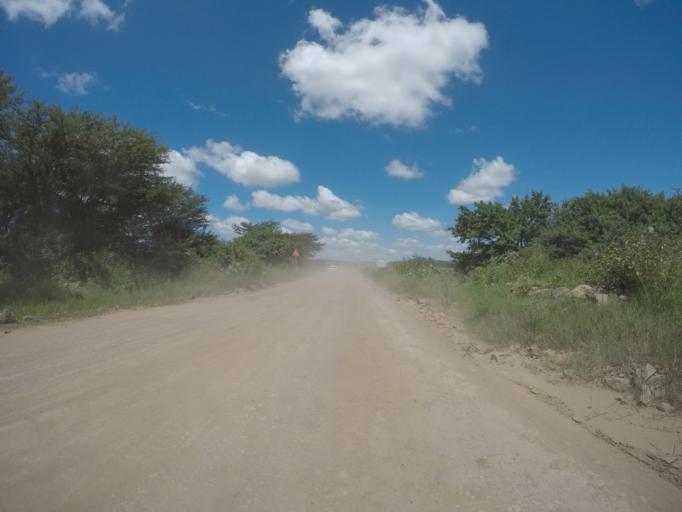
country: ZA
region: KwaZulu-Natal
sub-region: uThungulu District Municipality
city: Empangeni
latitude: -28.6608
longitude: 31.7781
